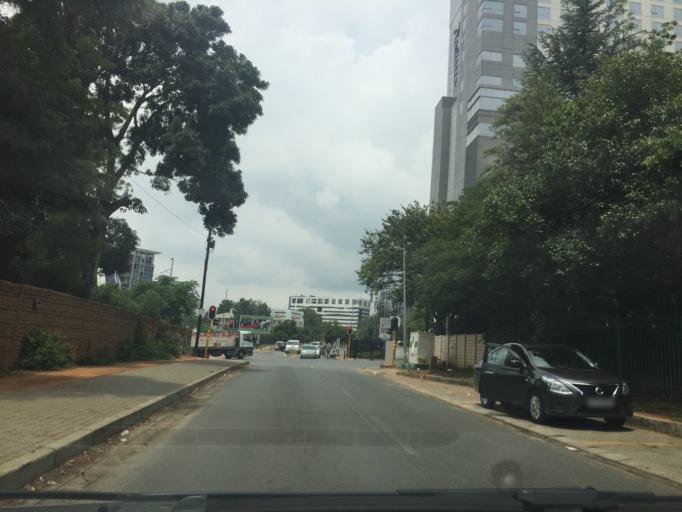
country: ZA
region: Gauteng
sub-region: City of Johannesburg Metropolitan Municipality
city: Johannesburg
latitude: -26.1035
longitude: 28.0623
